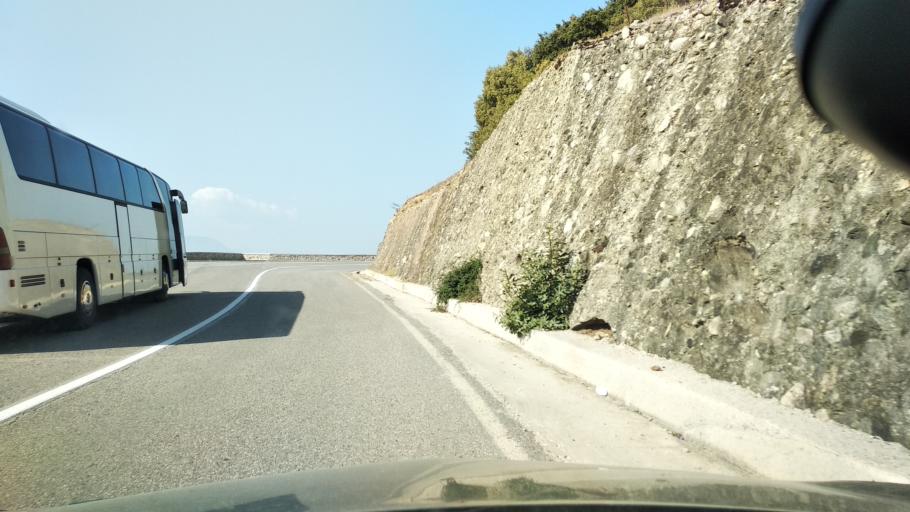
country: GR
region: Thessaly
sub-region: Trikala
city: Kalampaka
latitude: 39.7107
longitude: 21.6383
